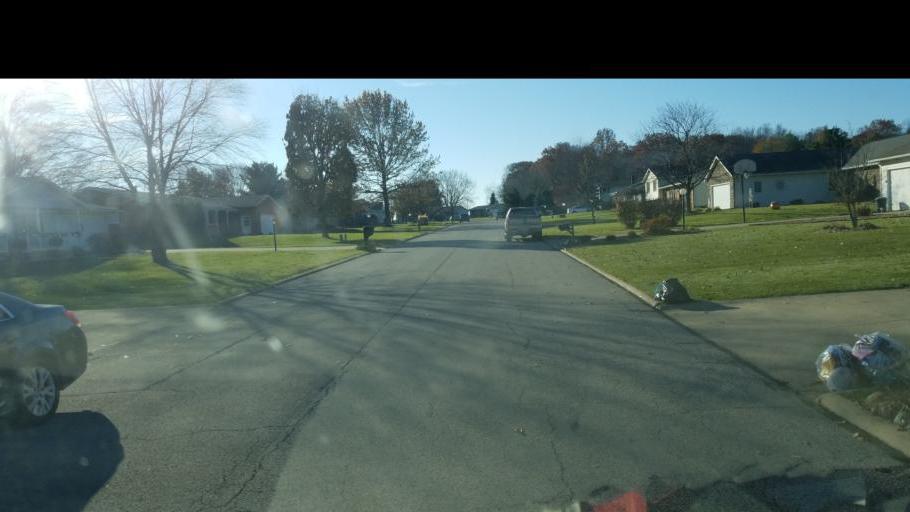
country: US
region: Ohio
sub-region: Ashland County
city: Ashland
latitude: 40.8389
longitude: -82.3363
